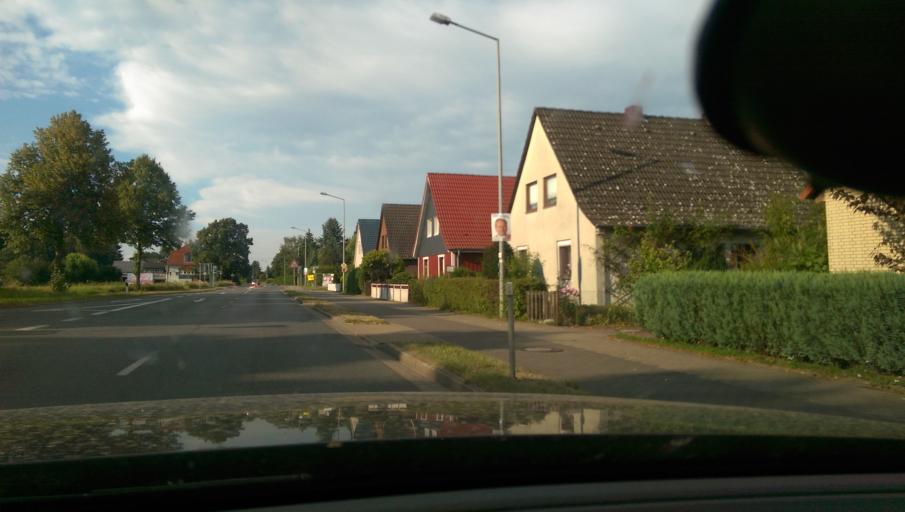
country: DE
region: Lower Saxony
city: Neustadt am Rubenberge
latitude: 52.4856
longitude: 9.4566
